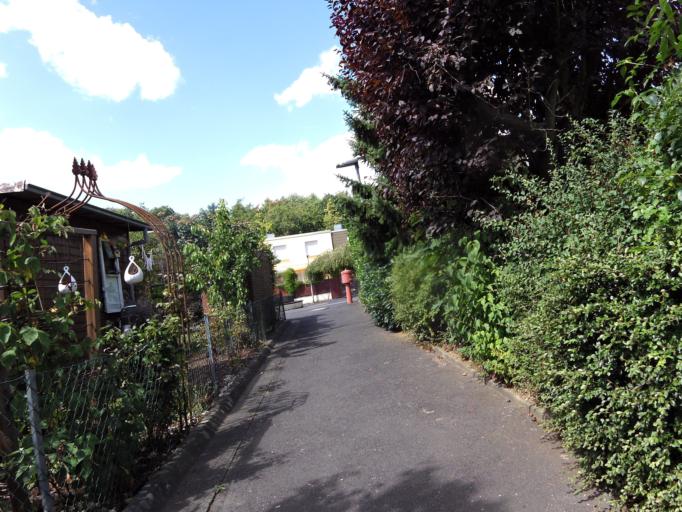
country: DE
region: Bavaria
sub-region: Regierungsbezirk Unterfranken
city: Hochberg
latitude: 49.7915
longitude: 9.8832
